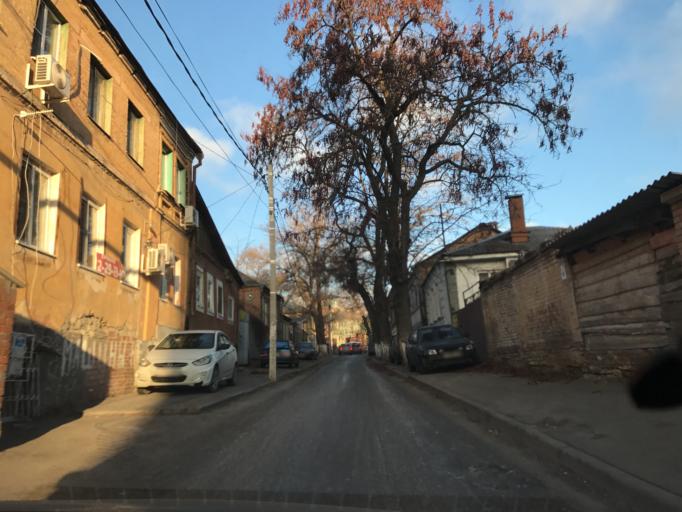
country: RU
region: Rostov
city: Rostov-na-Donu
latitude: 47.2186
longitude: 39.6845
